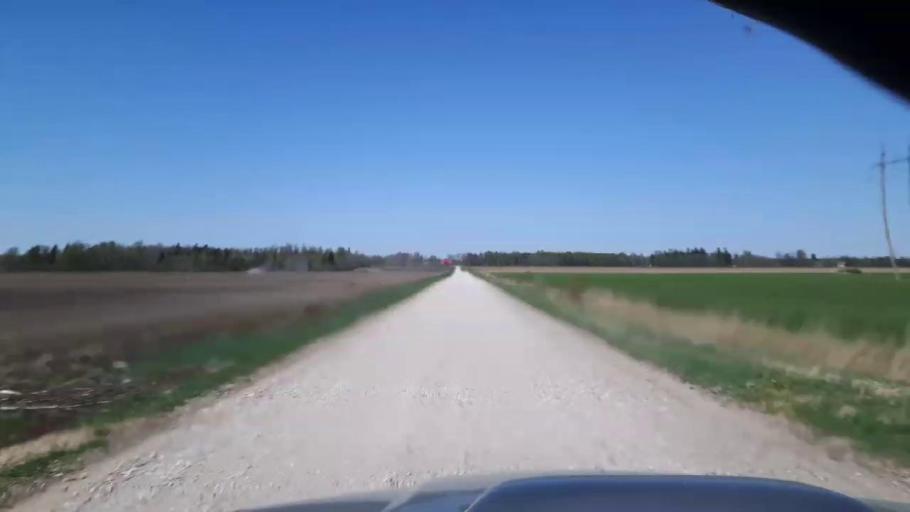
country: EE
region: Paernumaa
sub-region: Sindi linn
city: Sindi
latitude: 58.4771
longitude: 24.7452
